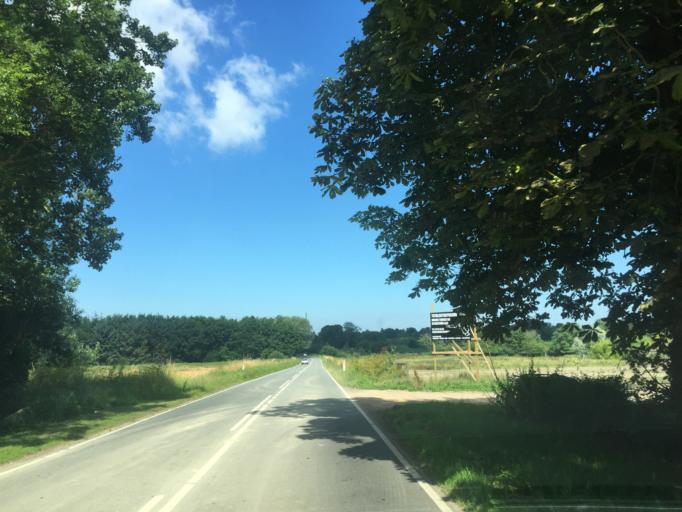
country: DK
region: South Denmark
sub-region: Nordfyns Kommune
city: Otterup
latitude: 55.5675
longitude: 10.3721
